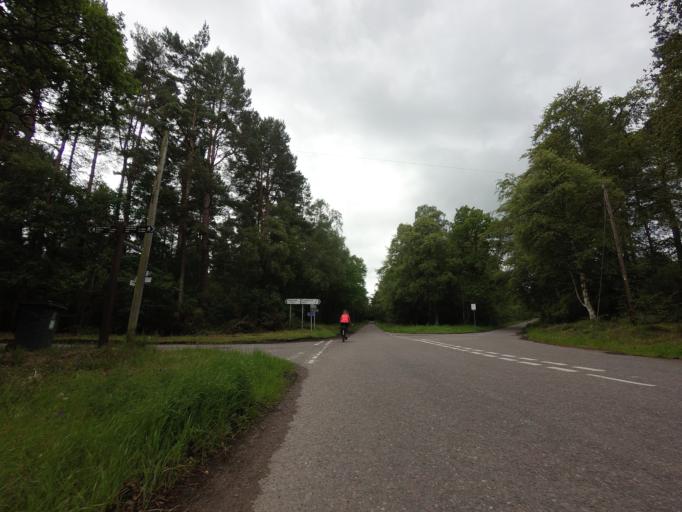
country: GB
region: Scotland
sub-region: Moray
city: Forres
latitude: 57.6188
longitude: -3.6760
